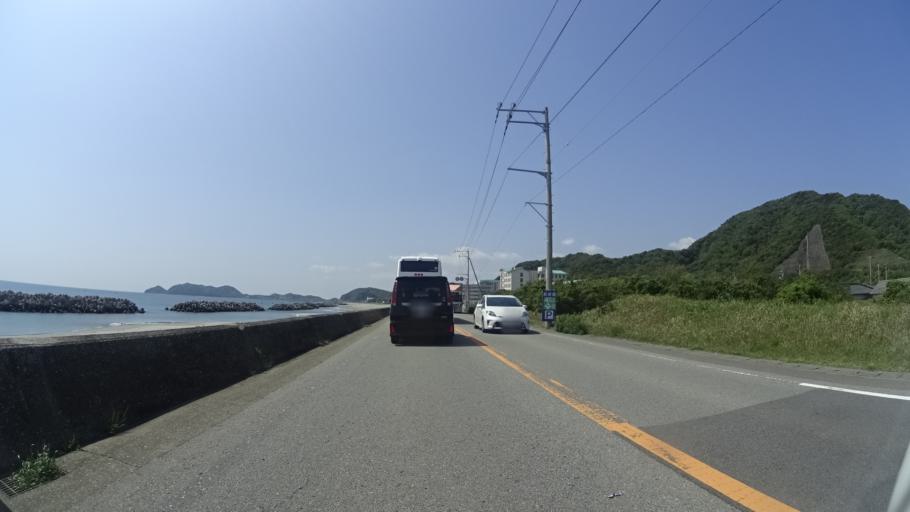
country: JP
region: Tokushima
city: Narutocho-mitsuishi
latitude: 34.2088
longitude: 134.6275
